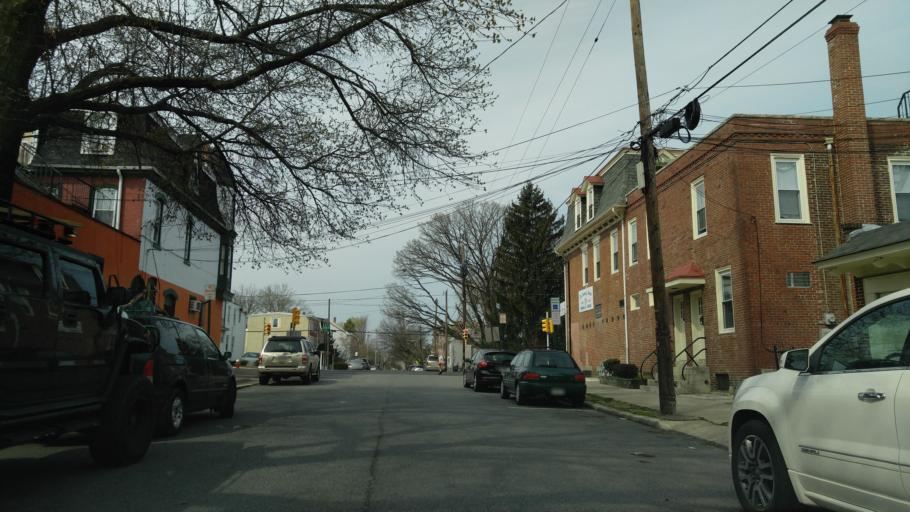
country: US
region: Pennsylvania
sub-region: Chester County
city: Phoenixville
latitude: 40.1301
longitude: -75.5173
